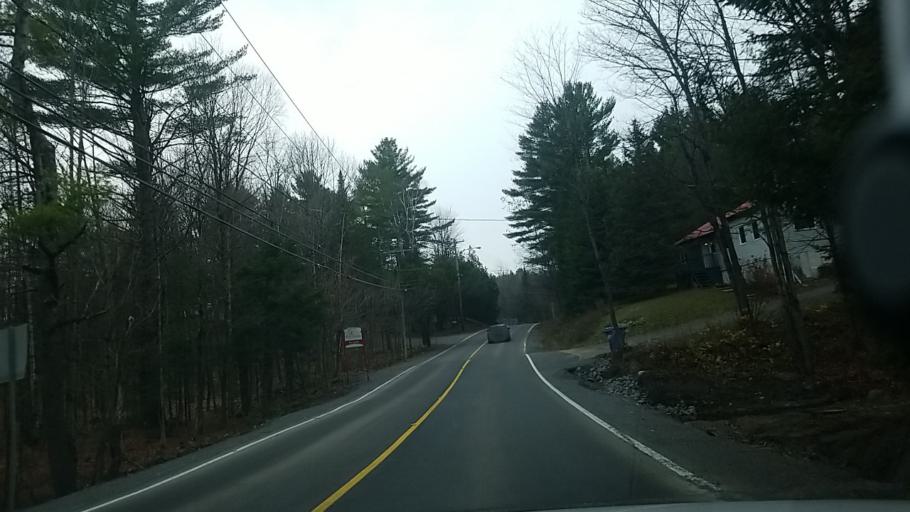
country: CA
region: Quebec
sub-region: Laurentides
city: Saint-Colomban
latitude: 45.7827
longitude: -74.1048
